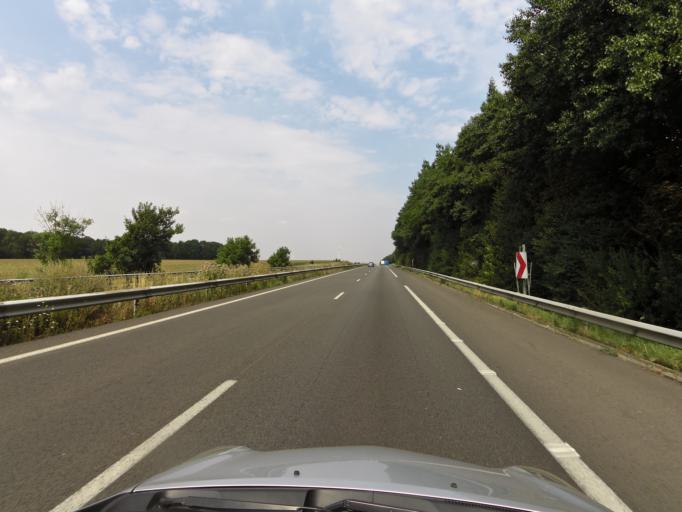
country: FR
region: Picardie
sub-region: Departement de l'Aisne
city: Holnon
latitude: 49.8758
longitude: 3.2461
